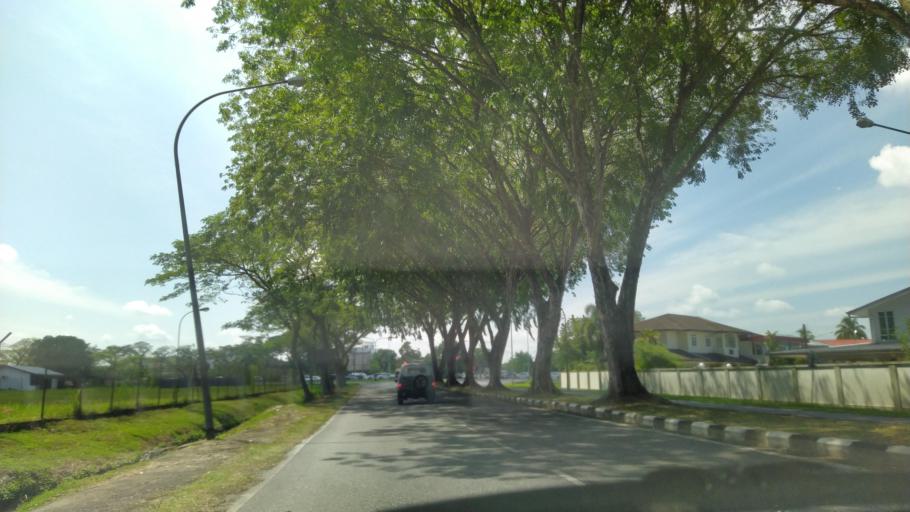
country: MY
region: Sarawak
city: Sibu
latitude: 2.3123
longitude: 111.8345
